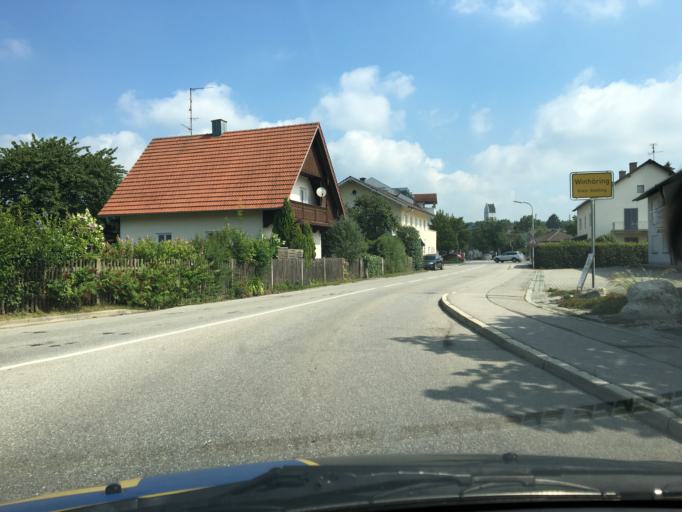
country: DE
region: Bavaria
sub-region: Upper Bavaria
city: Winhoring
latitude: 48.2636
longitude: 12.6503
